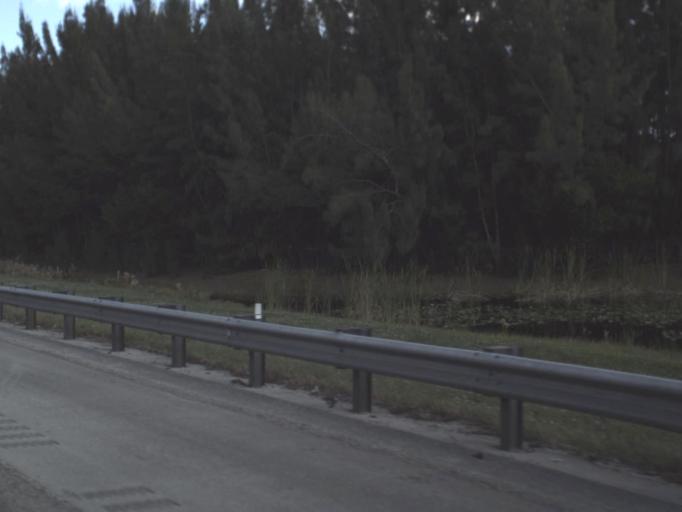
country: US
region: Florida
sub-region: Palm Beach County
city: Schall Circle
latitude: 26.7624
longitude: -80.1337
